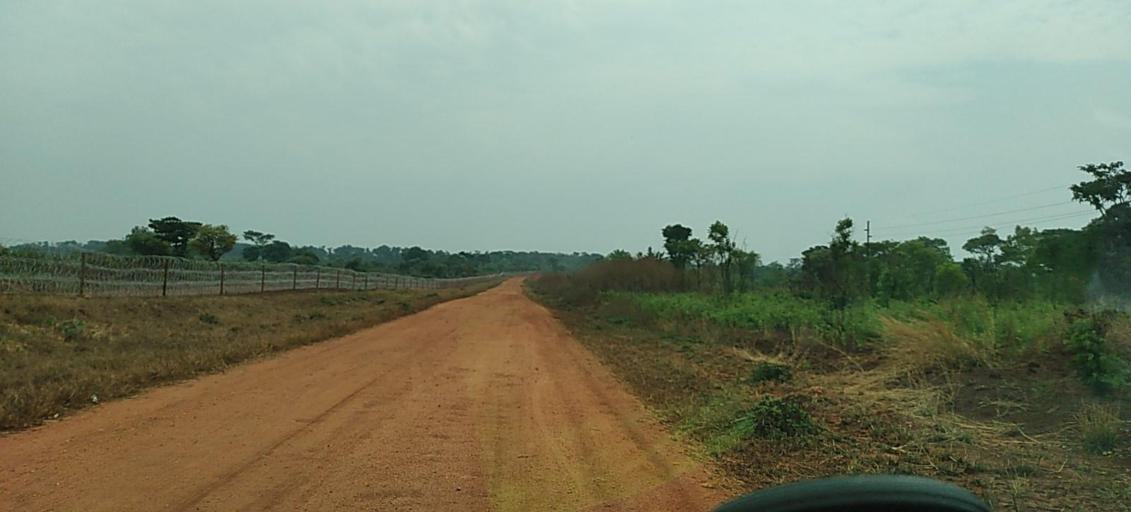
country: ZM
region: North-Western
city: Kansanshi
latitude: -12.1059
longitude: 26.4906
